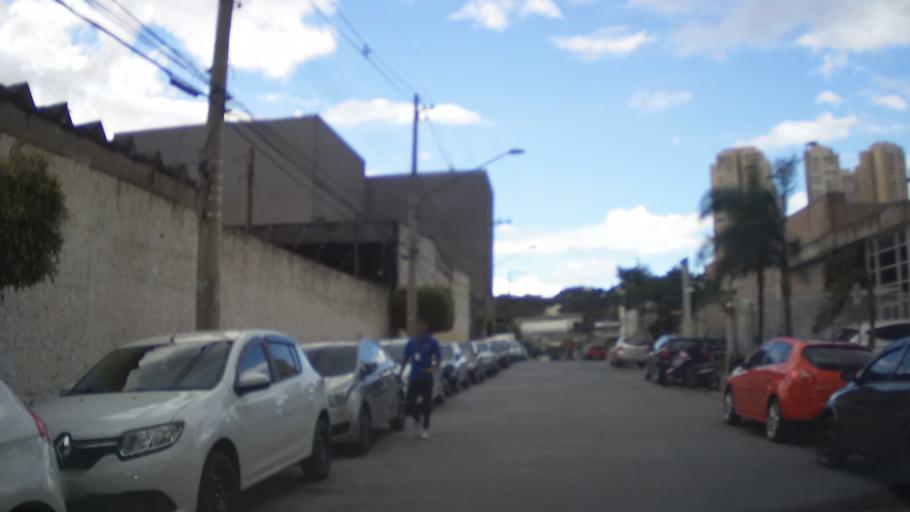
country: BR
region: Sao Paulo
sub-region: Guarulhos
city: Guarulhos
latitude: -23.4861
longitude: -46.5479
